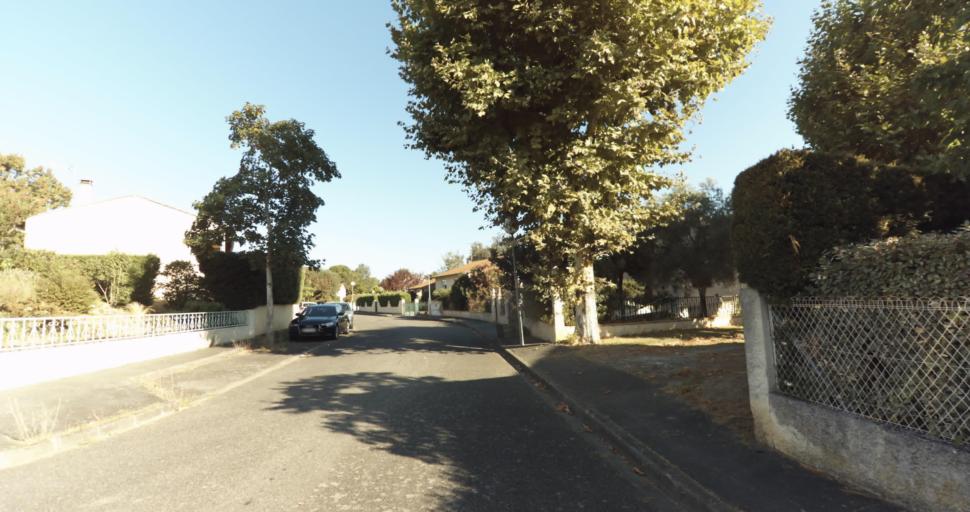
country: FR
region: Midi-Pyrenees
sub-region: Departement de la Haute-Garonne
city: Saint-Jean
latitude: 43.6559
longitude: 1.4959
